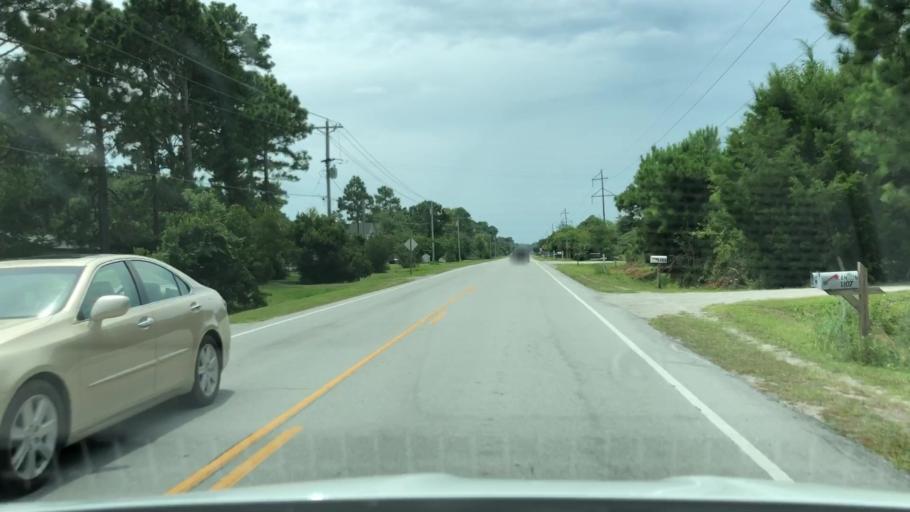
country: US
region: North Carolina
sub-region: Carteret County
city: Newport
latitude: 34.7447
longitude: -76.8817
